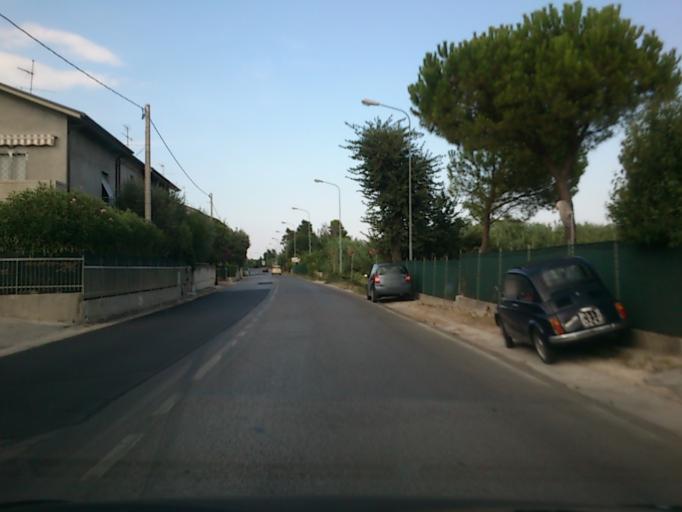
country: IT
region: The Marches
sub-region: Provincia di Pesaro e Urbino
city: Rosciano
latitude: 43.8062
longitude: 12.9798
